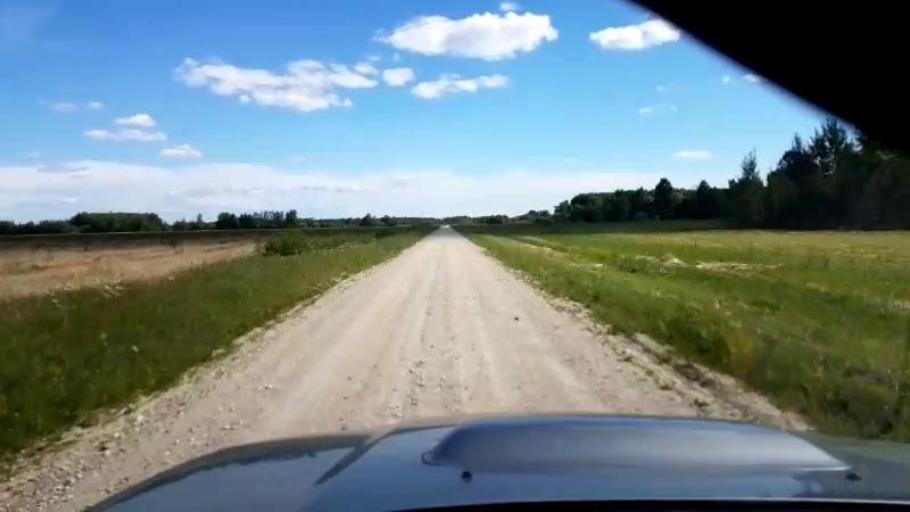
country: EE
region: Paernumaa
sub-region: Sauga vald
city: Sauga
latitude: 58.5027
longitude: 24.5236
